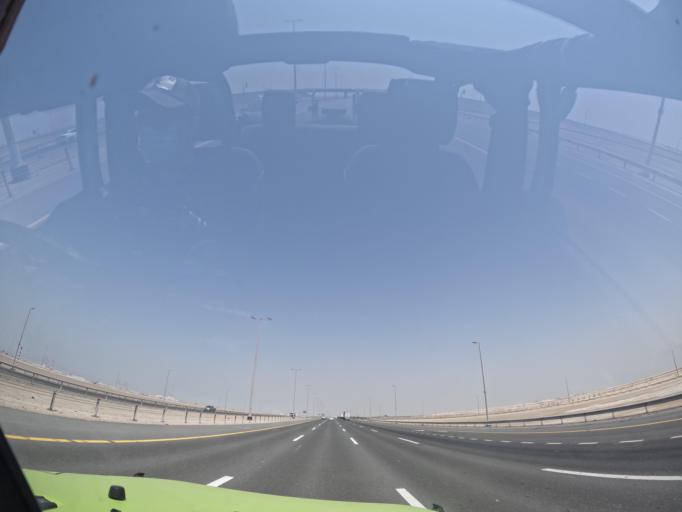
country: AE
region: Abu Dhabi
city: Abu Dhabi
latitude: 24.2490
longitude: 54.4760
